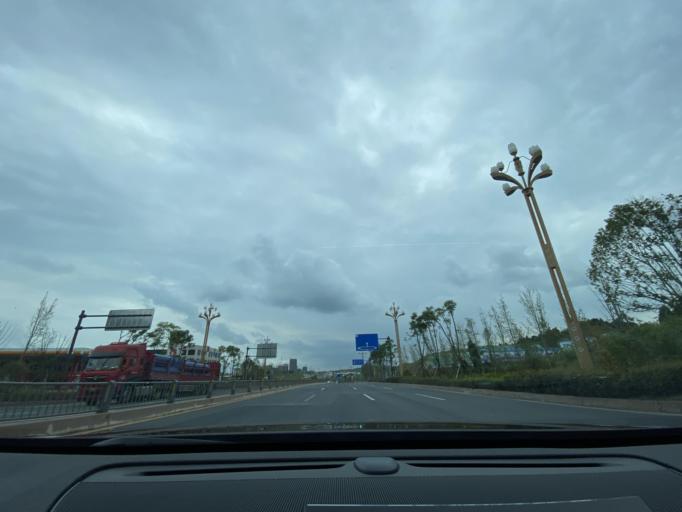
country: CN
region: Sichuan
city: Jiancheng
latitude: 30.4482
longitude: 104.4959
